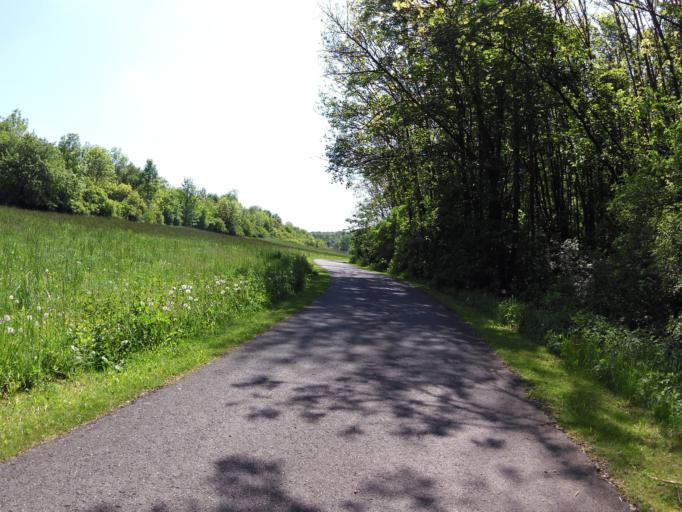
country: DE
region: Bavaria
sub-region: Regierungsbezirk Unterfranken
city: Eibelstadt
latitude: 49.7335
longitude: 10.0135
